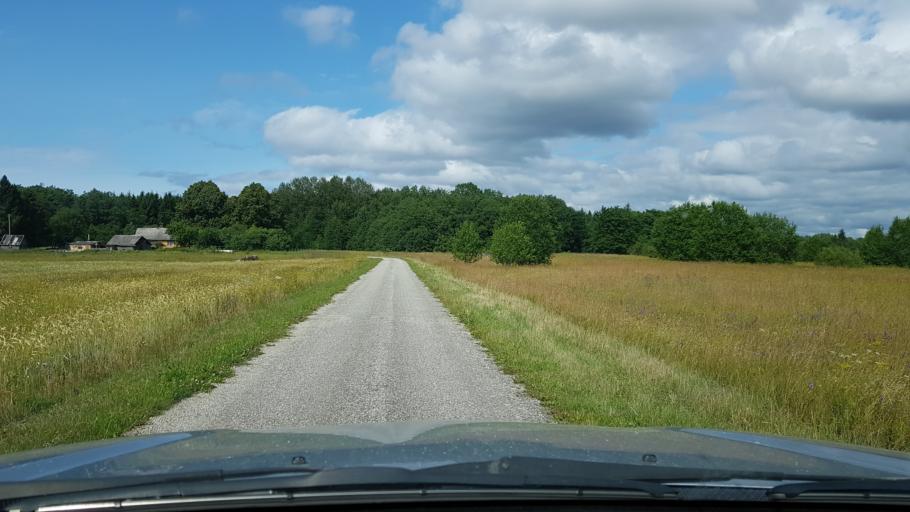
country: EE
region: Ida-Virumaa
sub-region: Narva-Joesuu linn
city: Narva-Joesuu
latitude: 59.3749
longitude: 27.9570
